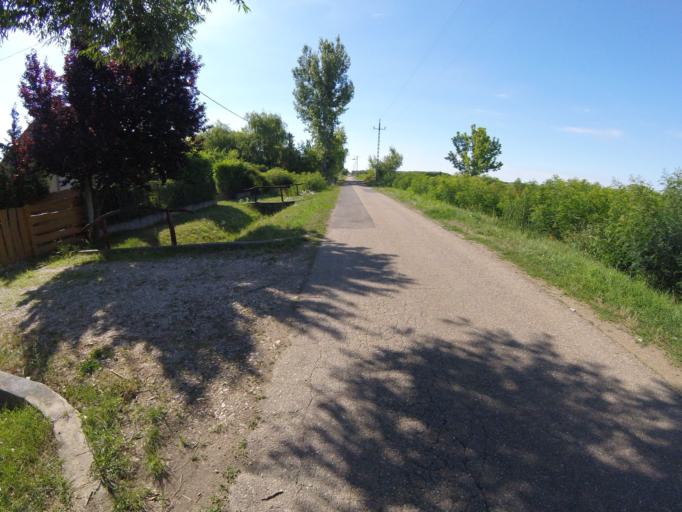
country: HU
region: Heves
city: Tiszanana
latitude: 47.5828
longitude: 20.6014
